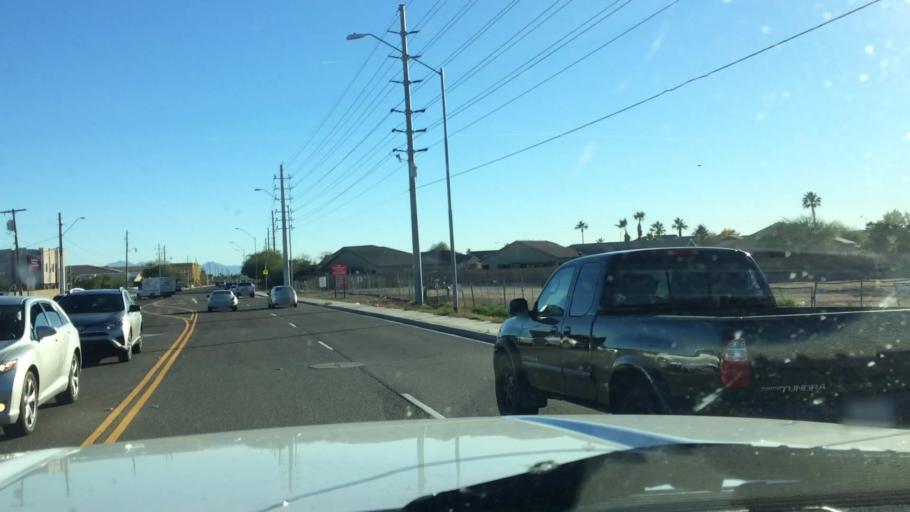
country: US
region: Arizona
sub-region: Maricopa County
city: Surprise
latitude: 33.6319
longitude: -112.3423
